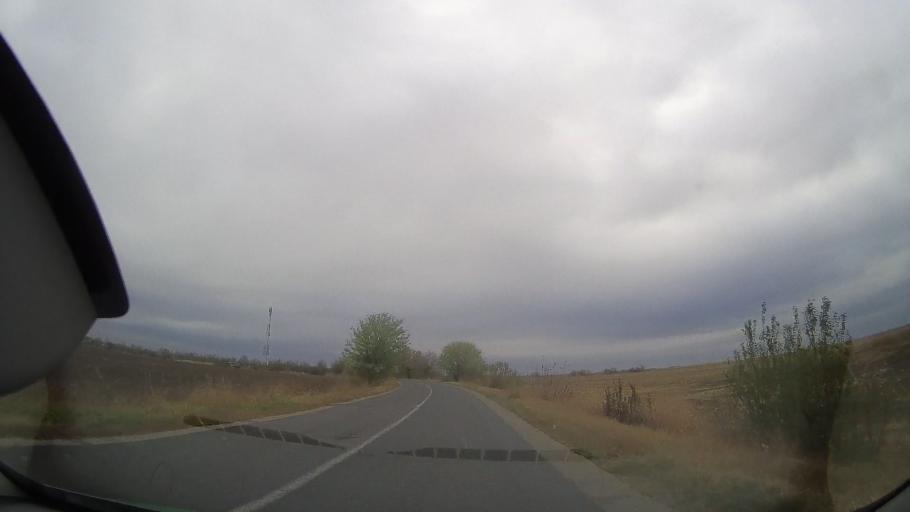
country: RO
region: Buzau
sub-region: Comuna Padina
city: Padina
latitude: 44.7792
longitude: 27.1540
